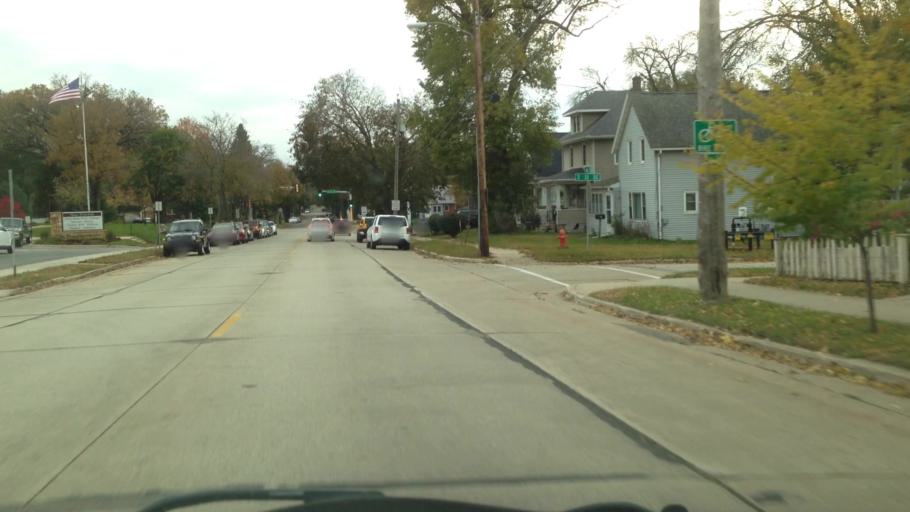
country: US
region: Minnesota
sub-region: Olmsted County
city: Rochester
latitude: 44.0207
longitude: -92.4488
